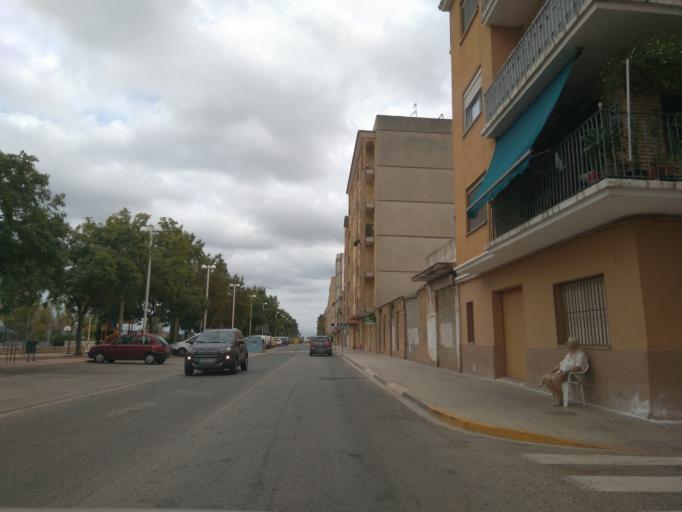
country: ES
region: Valencia
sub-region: Provincia de Valencia
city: Carlet
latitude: 39.2249
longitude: -0.5165
